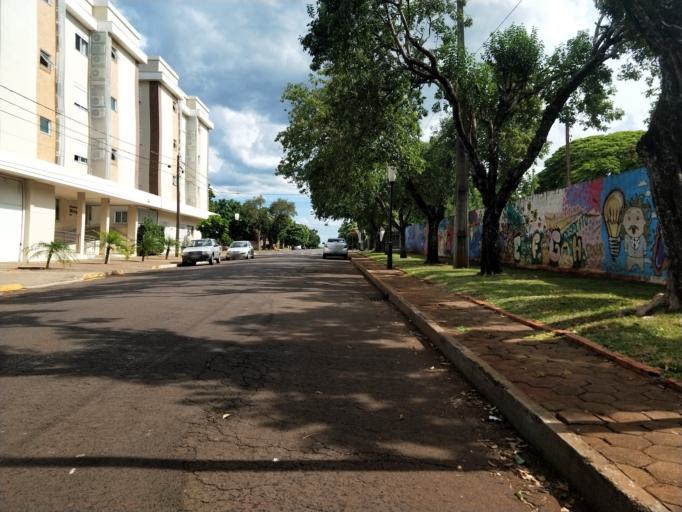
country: BR
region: Parana
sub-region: Marechal Candido Rondon
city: Marechal Candido Rondon
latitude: -24.5593
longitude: -54.0538
